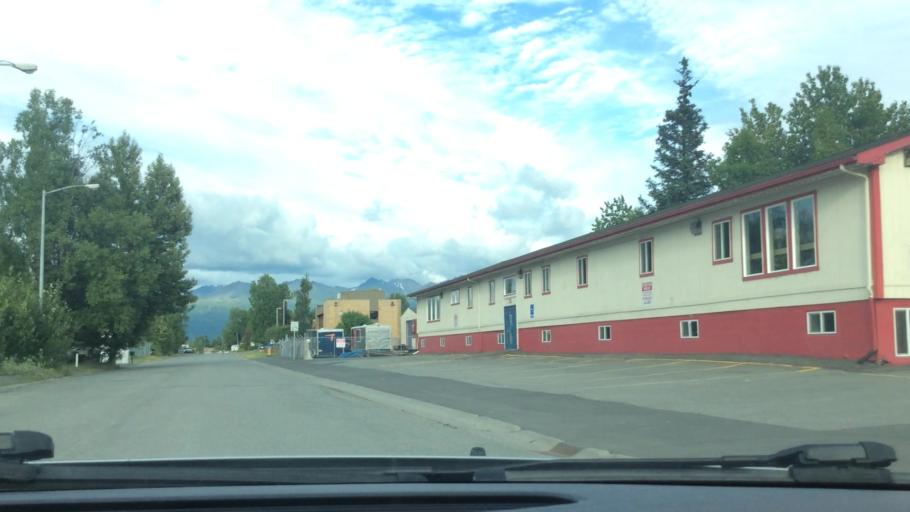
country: US
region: Alaska
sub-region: Anchorage Municipality
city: Anchorage
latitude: 61.1717
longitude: -149.8975
